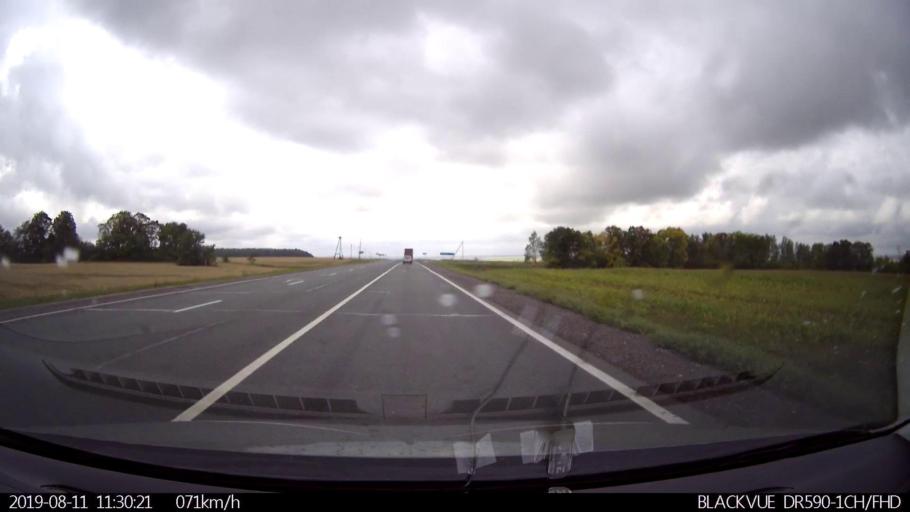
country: RU
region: Ulyanovsk
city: Krasnyy Gulyay
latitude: 54.0595
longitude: 48.2196
